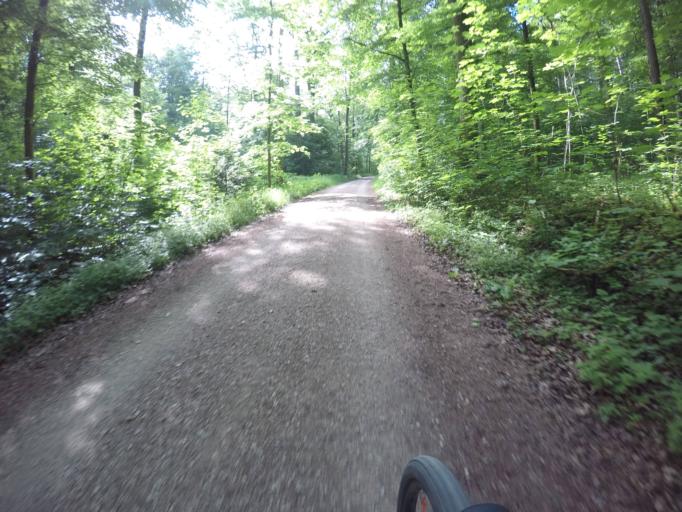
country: DE
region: Baden-Wuerttemberg
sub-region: Regierungsbezirk Stuttgart
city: Denkendorf
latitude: 48.6803
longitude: 9.3182
